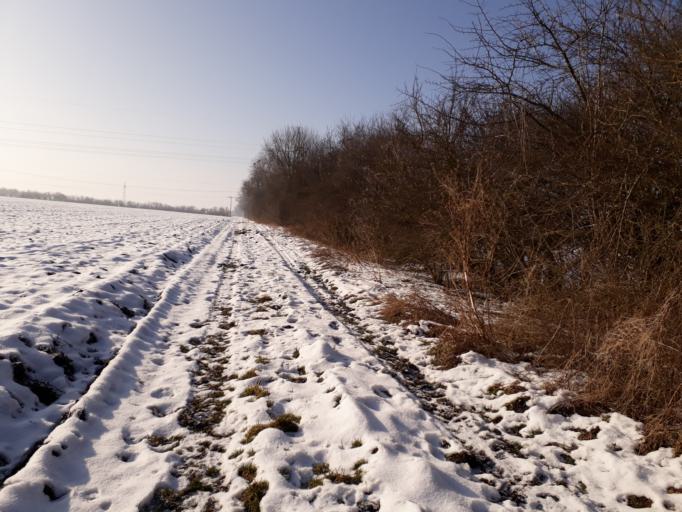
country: DE
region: Bavaria
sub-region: Upper Bavaria
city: Ismaning
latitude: 48.2007
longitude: 11.6875
